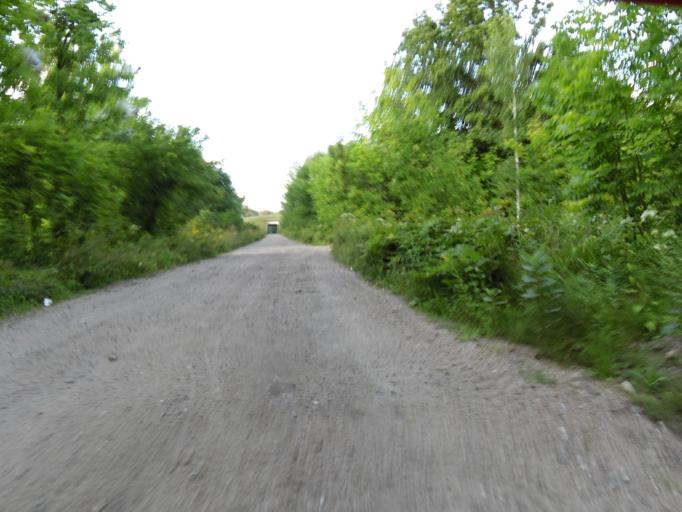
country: CA
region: Quebec
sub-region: Outaouais
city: Maniwaki
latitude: 46.3646
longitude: -75.9844
